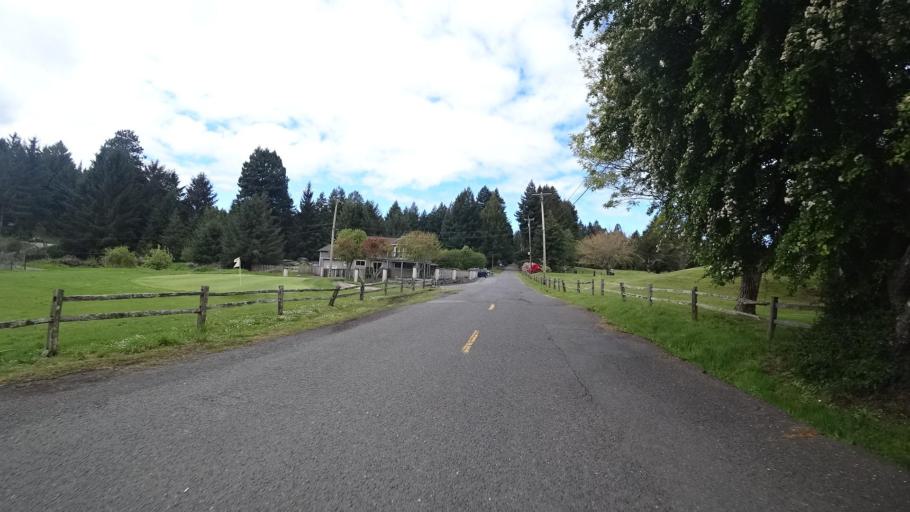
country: US
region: California
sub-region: Humboldt County
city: Bayside
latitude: 40.8460
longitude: -124.0490
